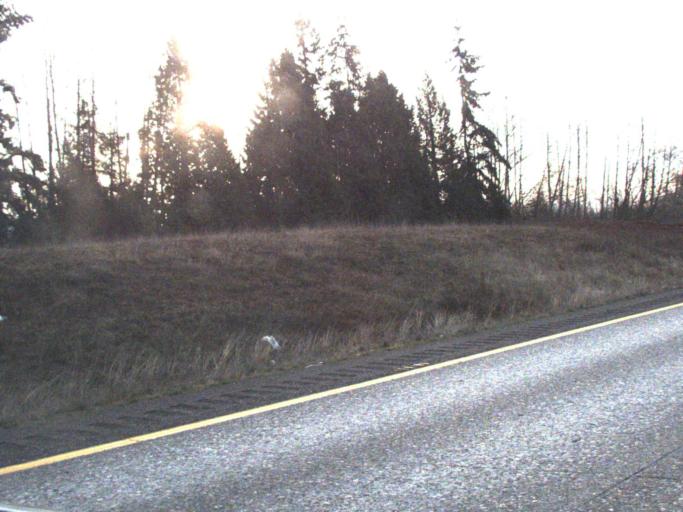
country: US
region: Washington
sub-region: Skagit County
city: Burlington
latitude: 48.5485
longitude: -122.3499
